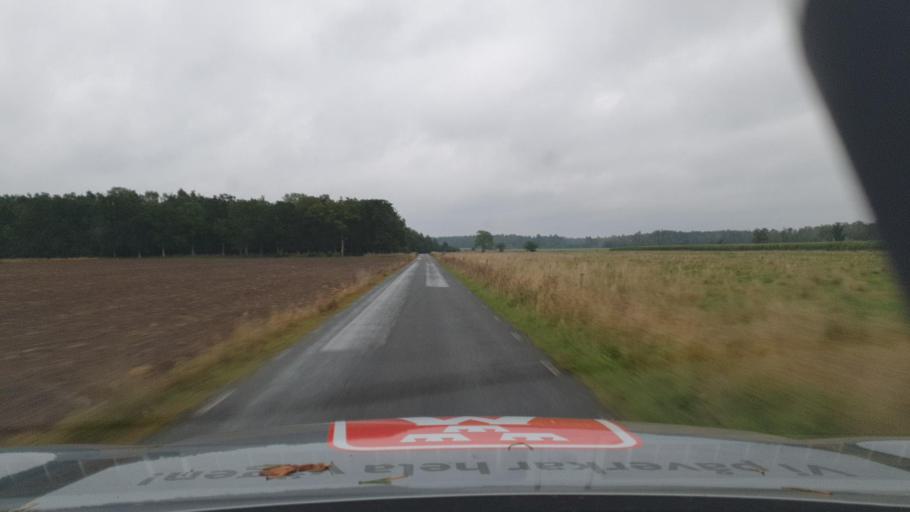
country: SE
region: Gotland
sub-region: Gotland
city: Klintehamn
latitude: 57.4351
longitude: 18.3943
